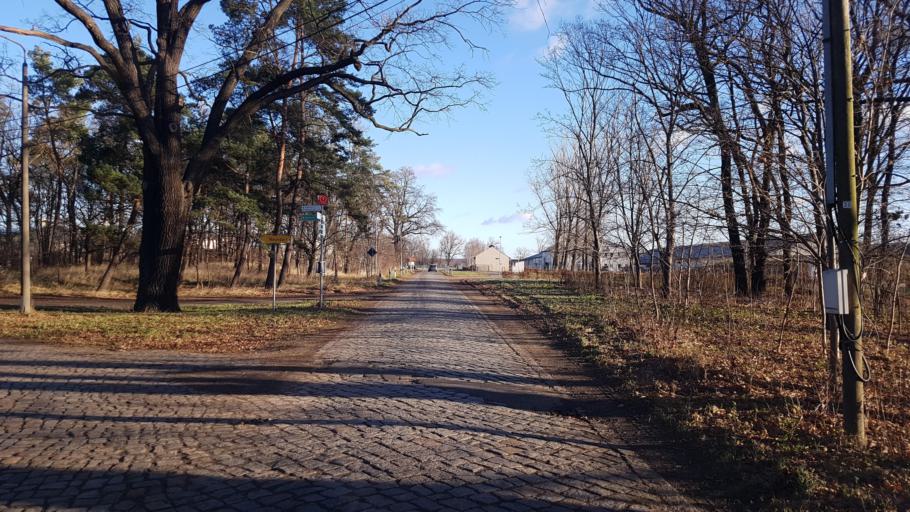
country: DE
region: Brandenburg
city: Forst
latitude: 51.7708
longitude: 14.6217
